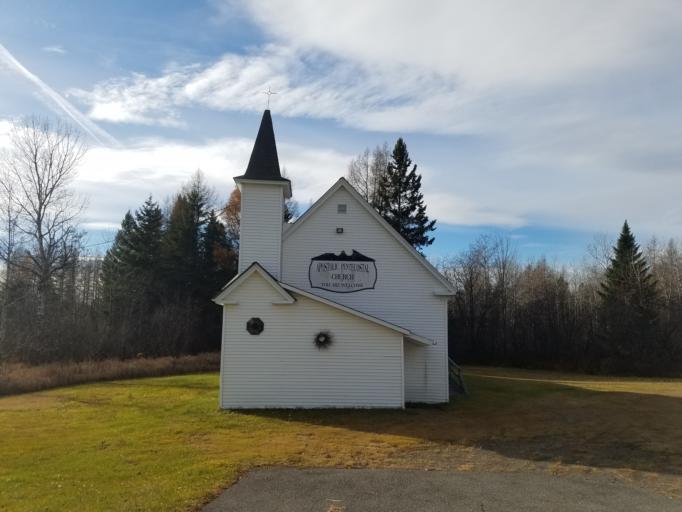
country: US
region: Maine
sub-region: Aroostook County
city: Presque Isle
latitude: 46.5794
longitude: -68.3826
